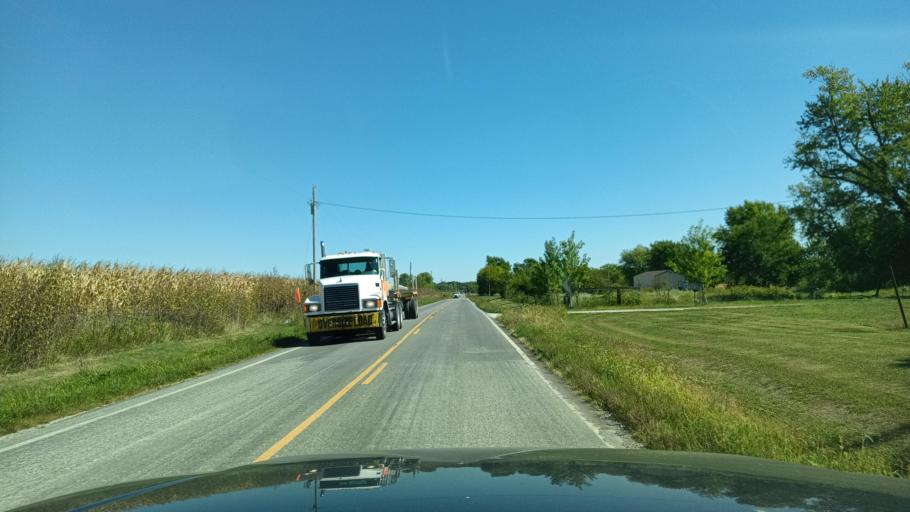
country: US
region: Missouri
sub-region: Macon County
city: La Plata
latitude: 40.0216
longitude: -92.5237
